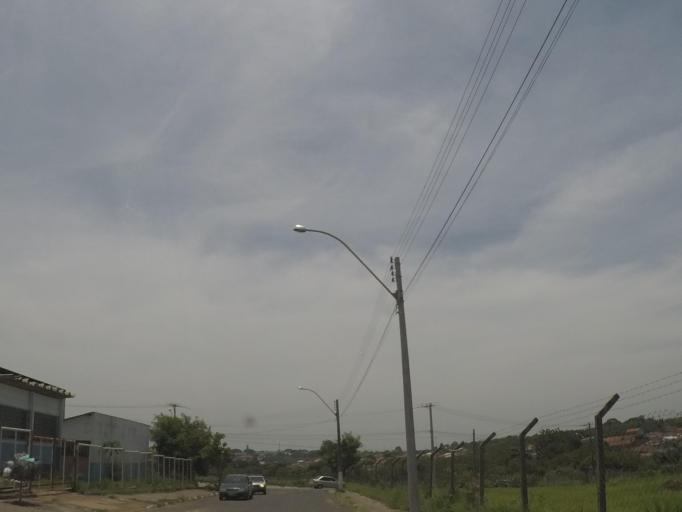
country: BR
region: Sao Paulo
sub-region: Hortolandia
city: Hortolandia
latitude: -22.8501
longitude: -47.1858
